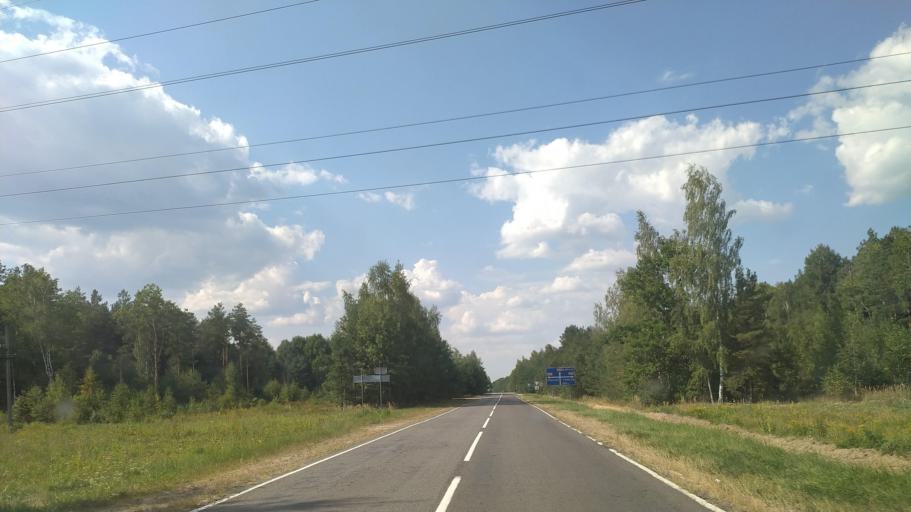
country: BY
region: Brest
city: Drahichyn
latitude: 52.2190
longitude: 25.1272
